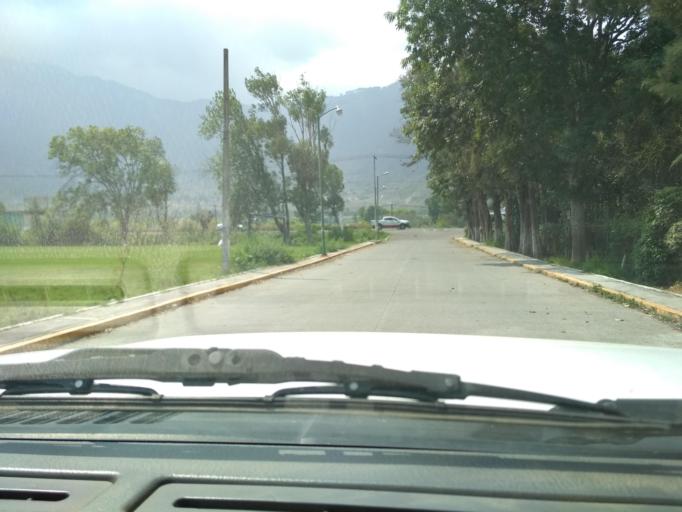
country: MX
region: Veracruz
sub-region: Acultzingo
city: Acatla
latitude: 18.7671
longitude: -97.2200
